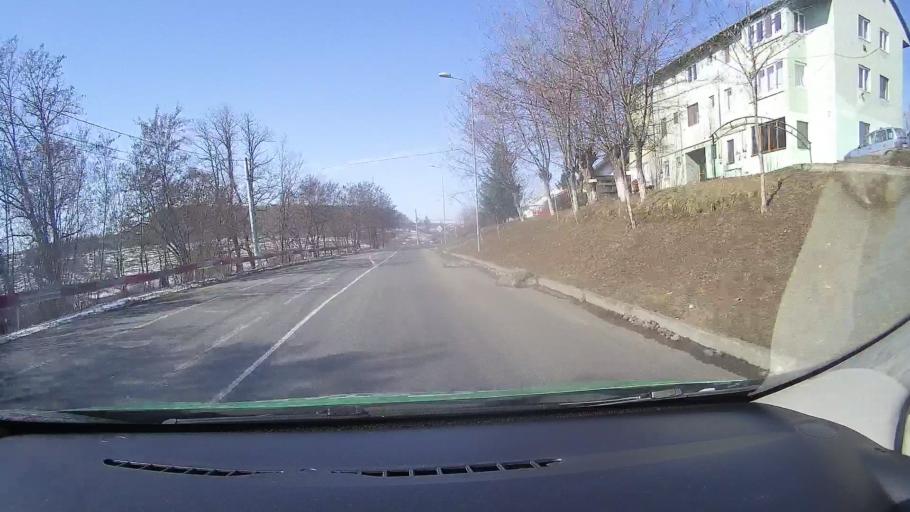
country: RO
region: Brasov
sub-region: Oras Rupea
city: Rupea
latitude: 46.0342
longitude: 25.2070
